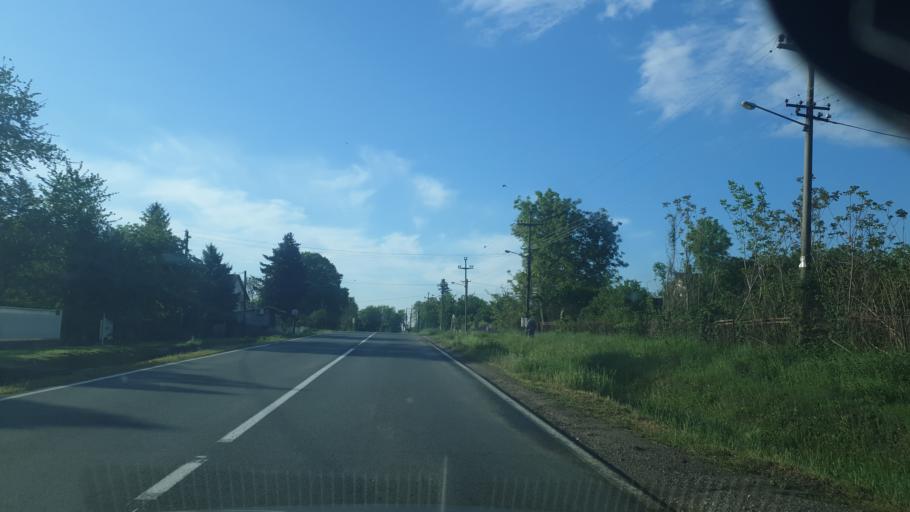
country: RS
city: Stubline
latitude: 44.5934
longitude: 20.1463
